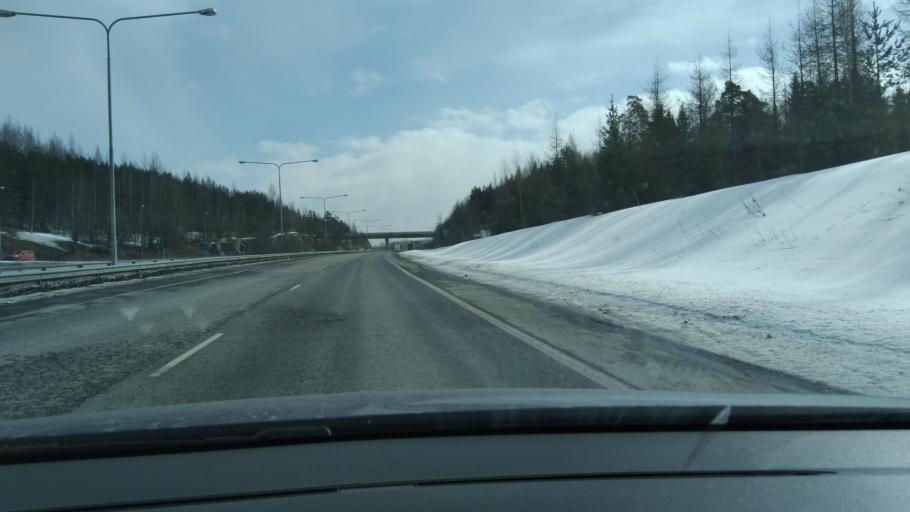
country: FI
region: Pirkanmaa
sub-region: Tampere
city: Tampere
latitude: 61.4622
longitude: 23.7751
